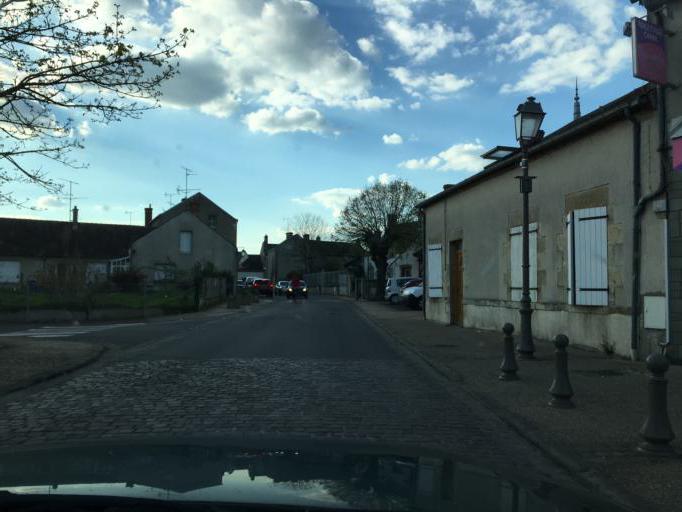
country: FR
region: Centre
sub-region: Departement du Loiret
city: Saint-Denis-en-Val
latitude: 47.8784
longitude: 1.9576
